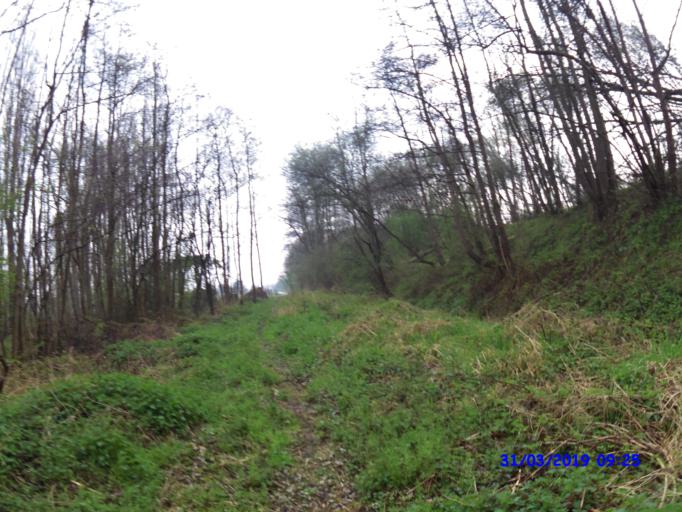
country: BE
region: Flanders
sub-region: Provincie Vlaams-Brabant
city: Liedekerke
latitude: 50.8836
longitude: 4.1094
